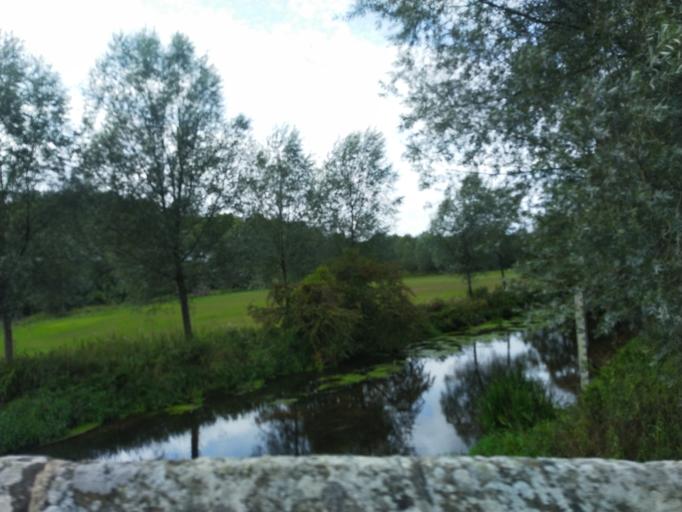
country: GB
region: England
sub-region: Dorset
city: Blandford Forum
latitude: 50.8176
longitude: -2.1164
